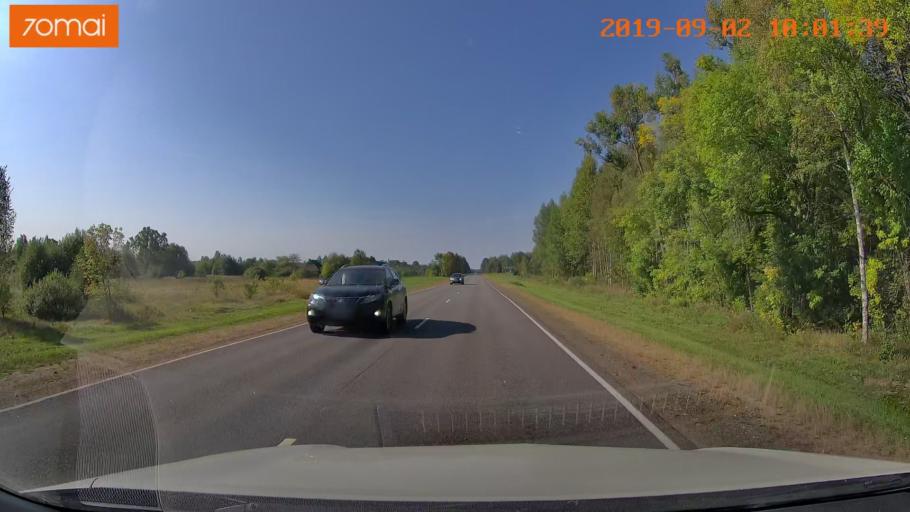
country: RU
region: Kaluga
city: Baryatino
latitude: 54.5176
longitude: 34.4935
